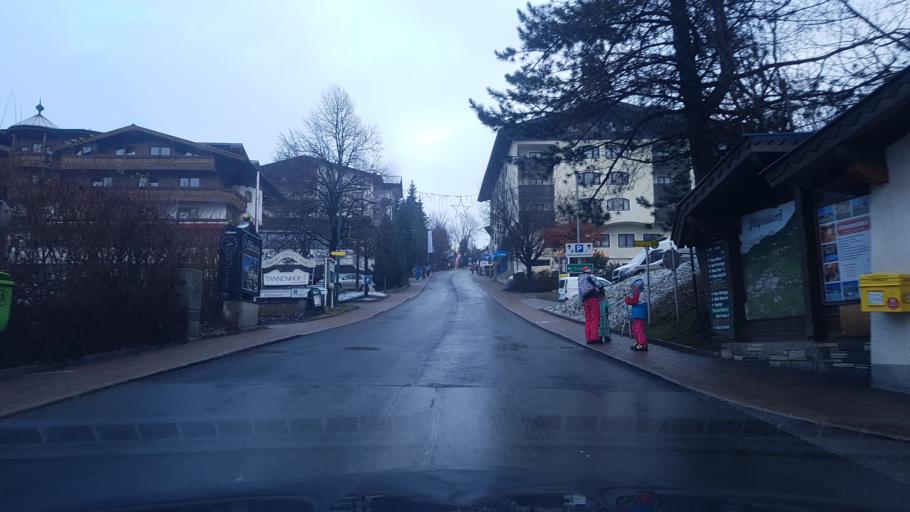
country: AT
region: Salzburg
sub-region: Politischer Bezirk Sankt Johann im Pongau
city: Sankt Johann im Pongau
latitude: 47.3221
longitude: 13.1946
